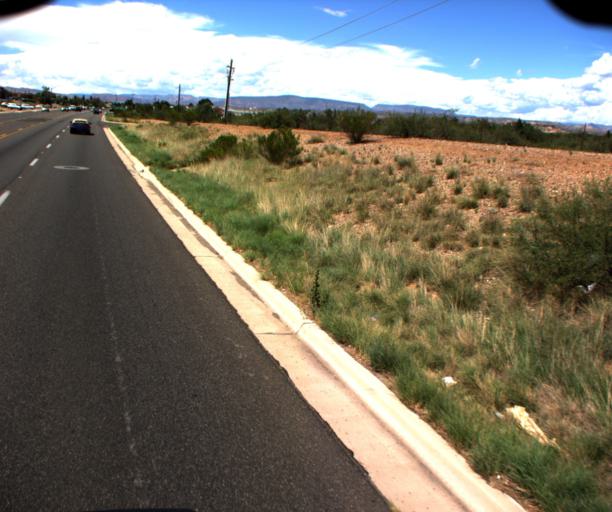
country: US
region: Arizona
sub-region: Yavapai County
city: Verde Village
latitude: 34.7157
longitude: -111.9999
